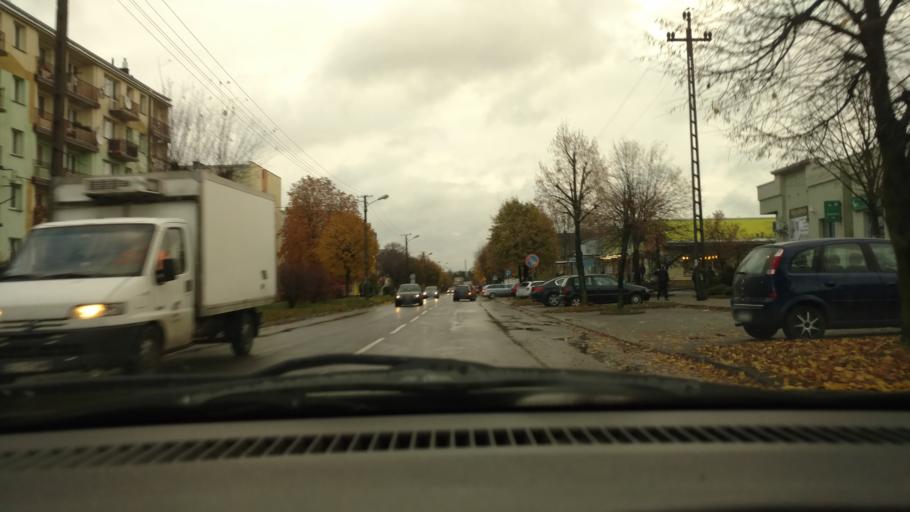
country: PL
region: Lodz Voivodeship
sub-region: Powiat laski
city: Lask
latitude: 51.5880
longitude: 19.1333
